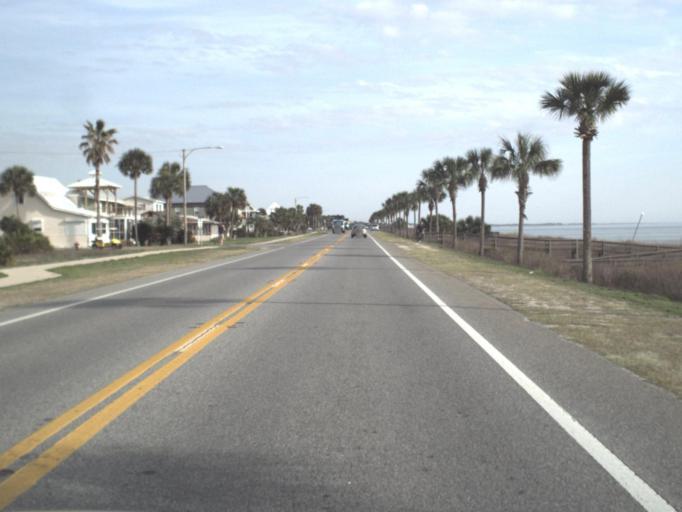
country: US
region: Florida
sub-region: Bay County
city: Mexico Beach
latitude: 29.9340
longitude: -85.3988
